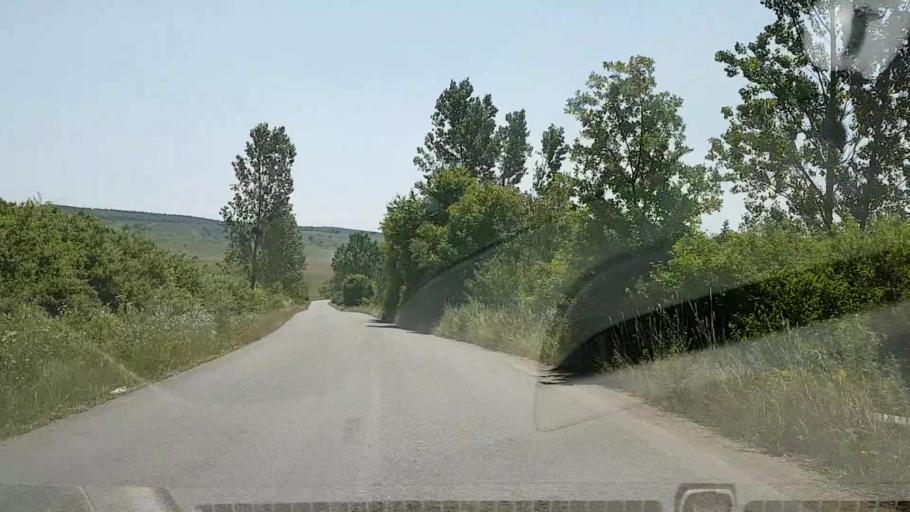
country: RO
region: Brasov
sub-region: Comuna Cincu
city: Cincu
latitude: 45.9338
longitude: 24.7908
